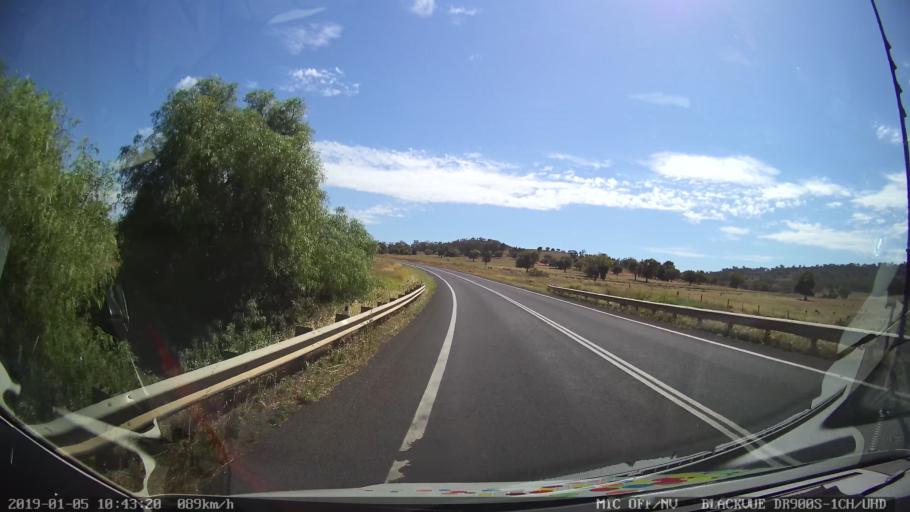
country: AU
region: New South Wales
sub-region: Warrumbungle Shire
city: Coonabarabran
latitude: -31.4659
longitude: 148.9870
